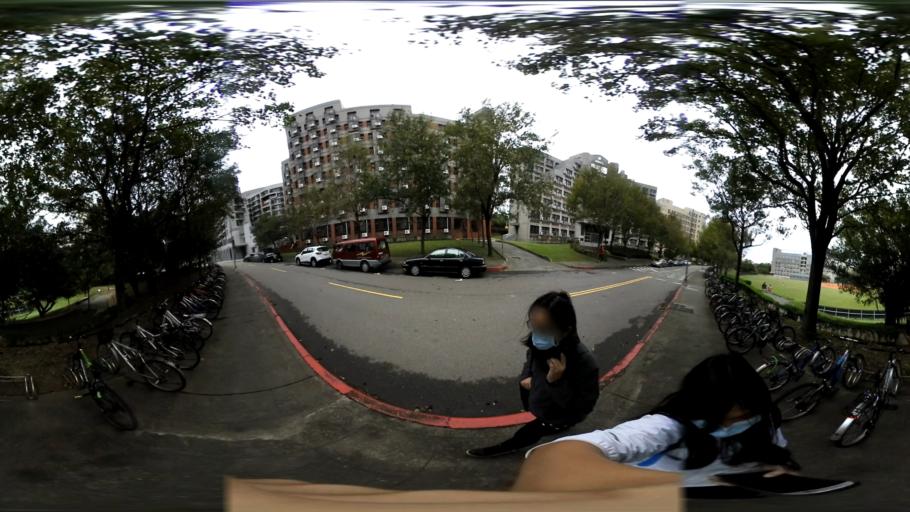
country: TW
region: Taiwan
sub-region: Hsinchu
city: Hsinchu
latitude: 24.7843
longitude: 120.9962
